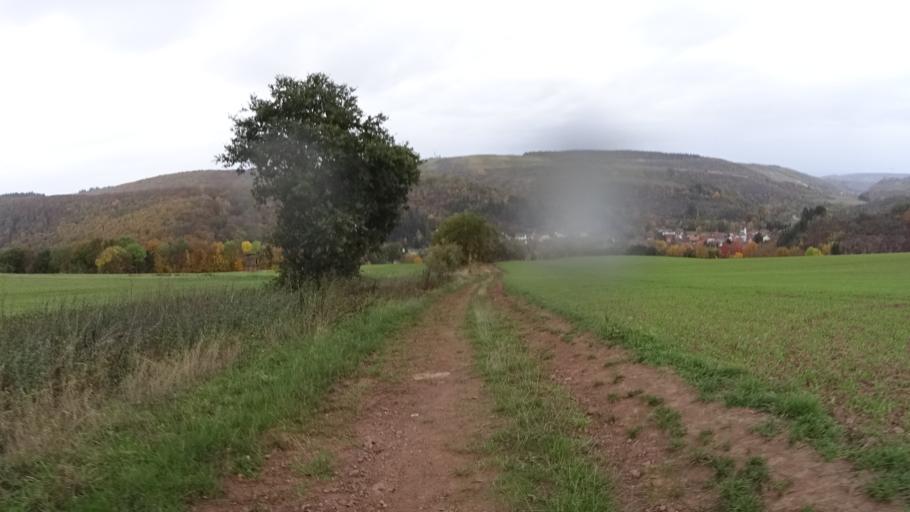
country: DE
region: Rheinland-Pfalz
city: Hochstatten
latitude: 49.7580
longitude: 7.8356
